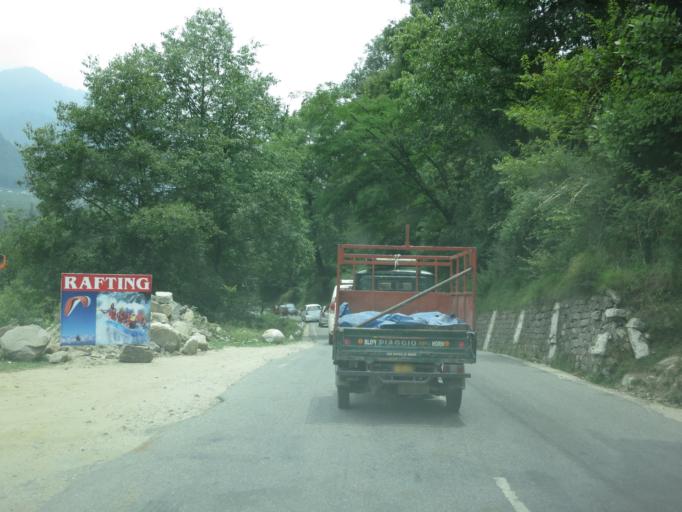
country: IN
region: Himachal Pradesh
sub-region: Kulu
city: Nagar
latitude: 32.1960
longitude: 77.1883
